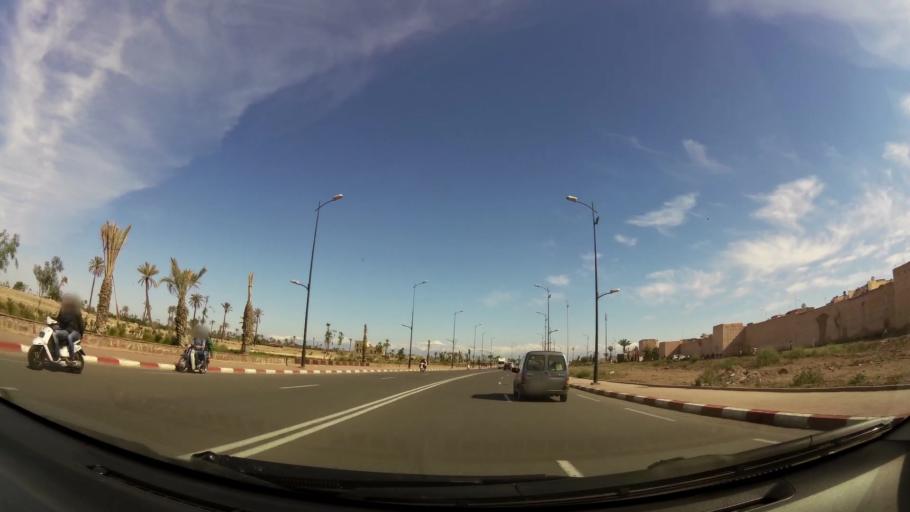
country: MA
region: Marrakech-Tensift-Al Haouz
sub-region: Marrakech
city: Marrakesh
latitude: 31.6316
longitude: -7.9739
